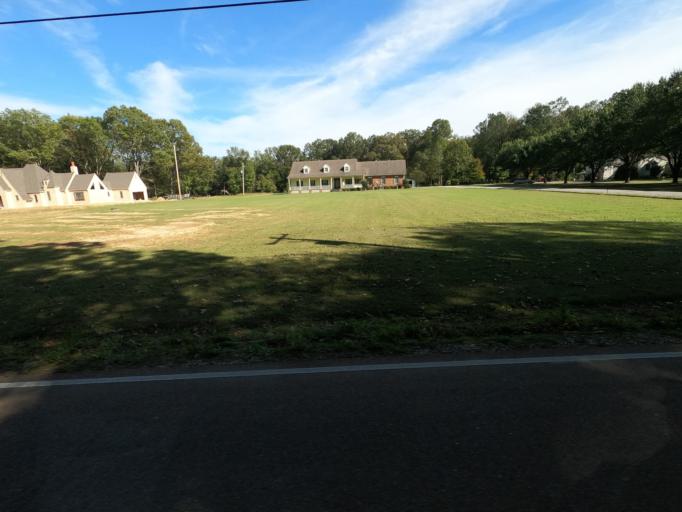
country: US
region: Tennessee
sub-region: Fayette County
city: Hickory Withe
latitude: 35.2150
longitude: -89.6504
